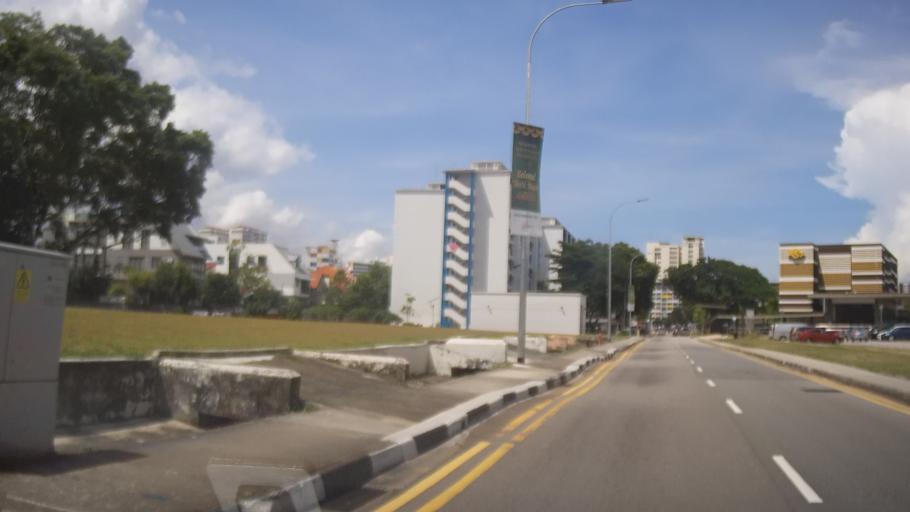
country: SG
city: Singapore
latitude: 1.3276
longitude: 103.8817
